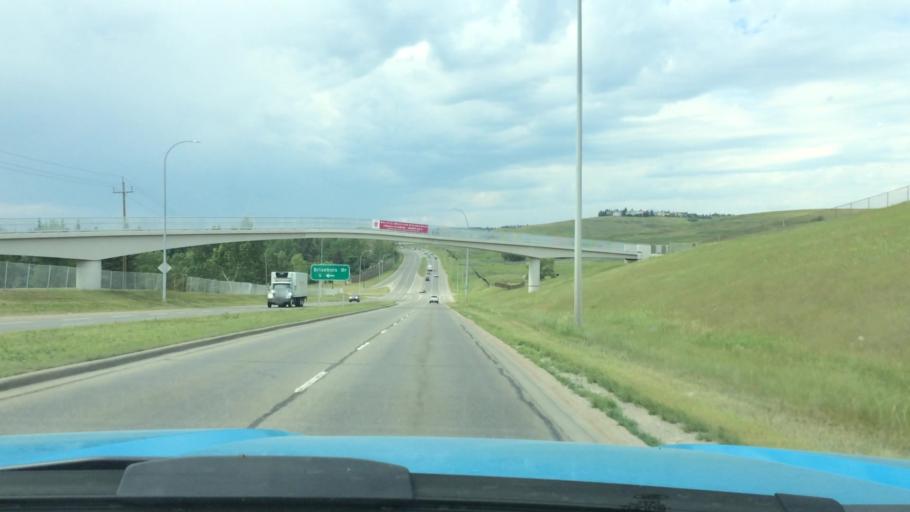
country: CA
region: Alberta
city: Calgary
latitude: 51.1012
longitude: -114.1236
